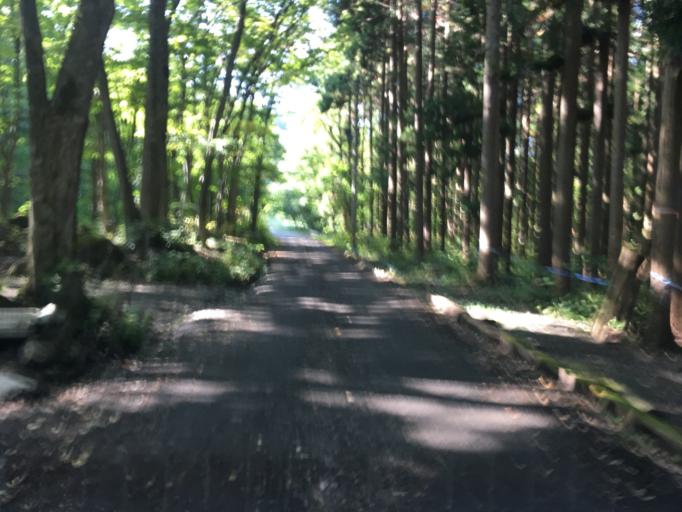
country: JP
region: Yamagata
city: Yonezawa
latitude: 37.8275
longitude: 140.2152
